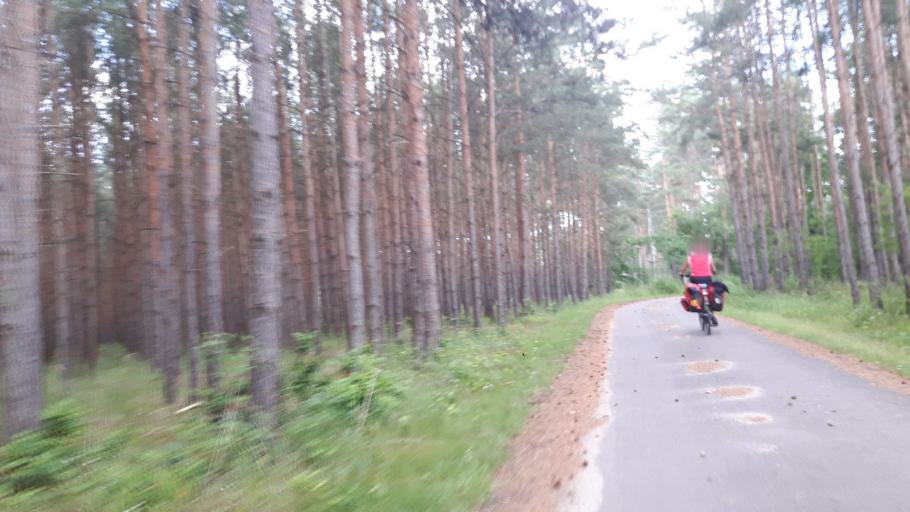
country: DE
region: Saxony-Anhalt
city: Radis
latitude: 51.7801
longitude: 12.5407
